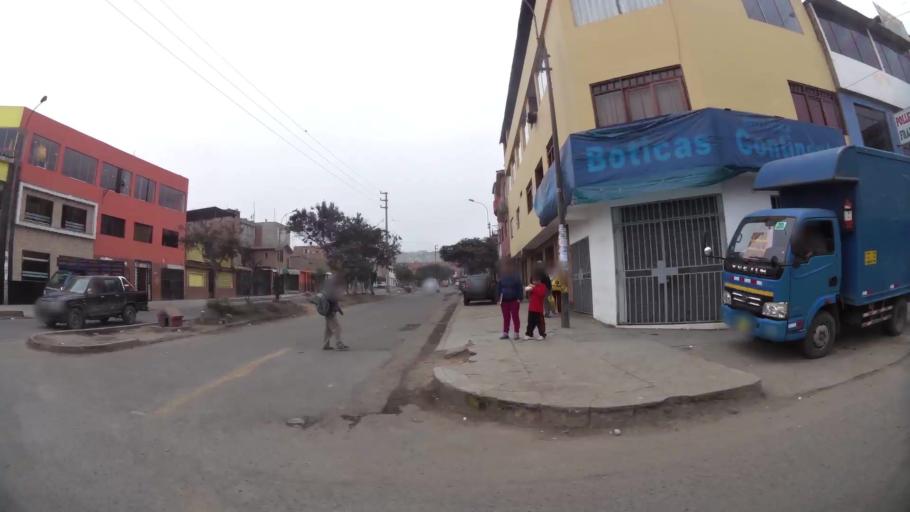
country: PE
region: Lima
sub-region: Lima
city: Surco
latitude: -12.1726
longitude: -76.9676
